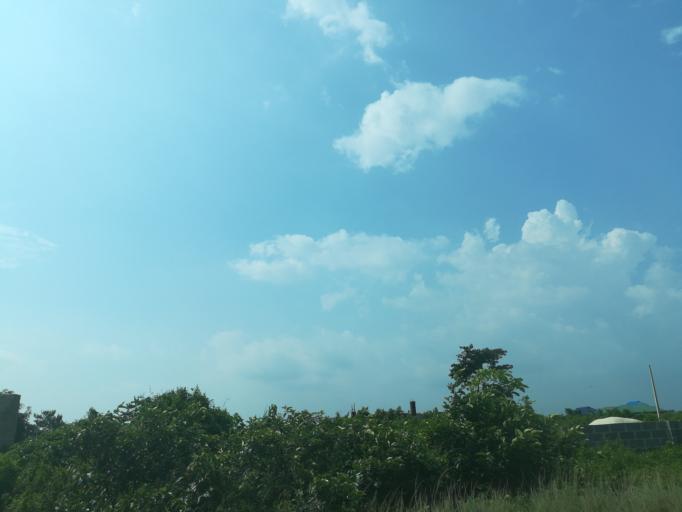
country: NG
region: Lagos
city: Ikorodu
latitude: 6.6176
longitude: 3.6503
